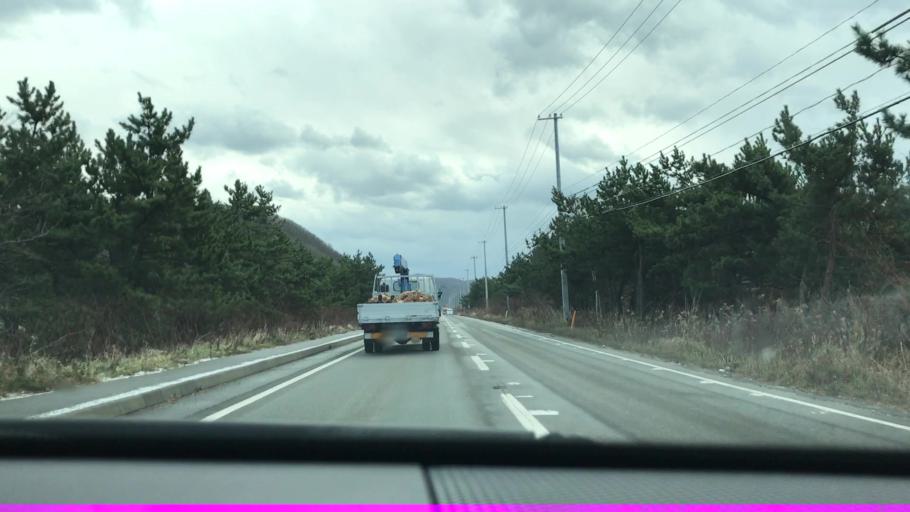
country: JP
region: Hokkaido
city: Shizunai-furukawacho
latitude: 42.3081
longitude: 142.4388
